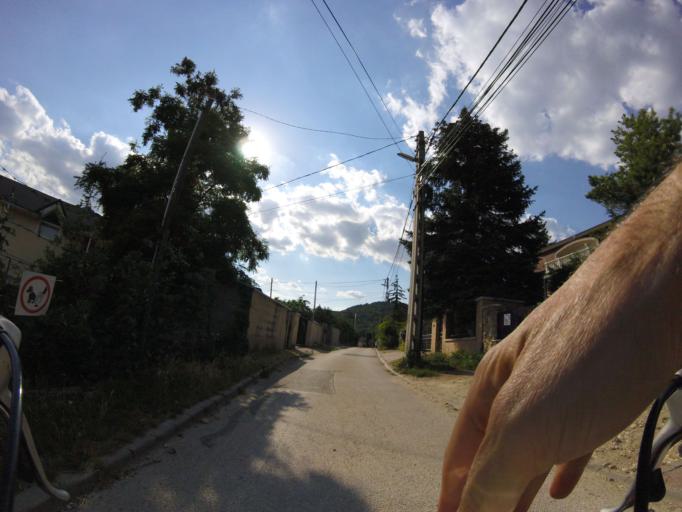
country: HU
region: Pest
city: Budaors
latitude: 47.4609
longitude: 18.9292
